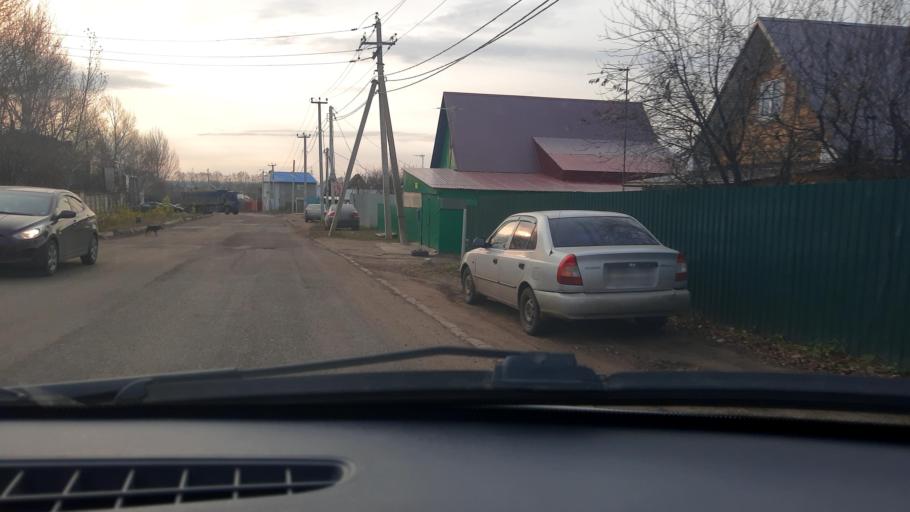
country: RU
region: Bashkortostan
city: Avdon
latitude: 54.6837
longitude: 55.7957
